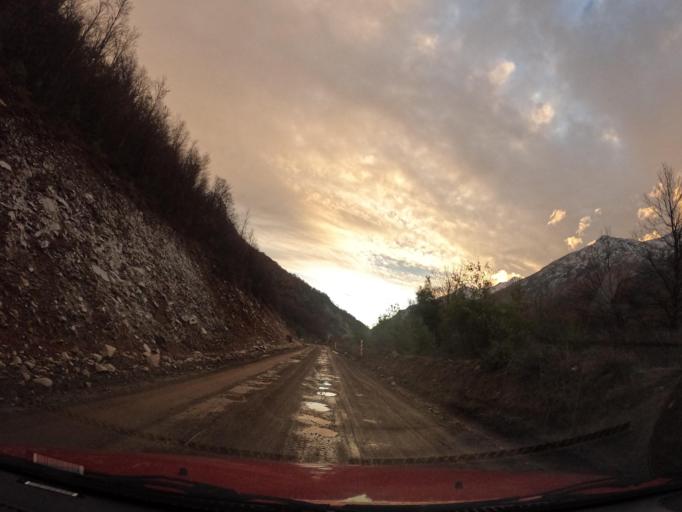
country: CL
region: Maule
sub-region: Provincia de Linares
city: Colbun
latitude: -35.8582
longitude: -71.1530
